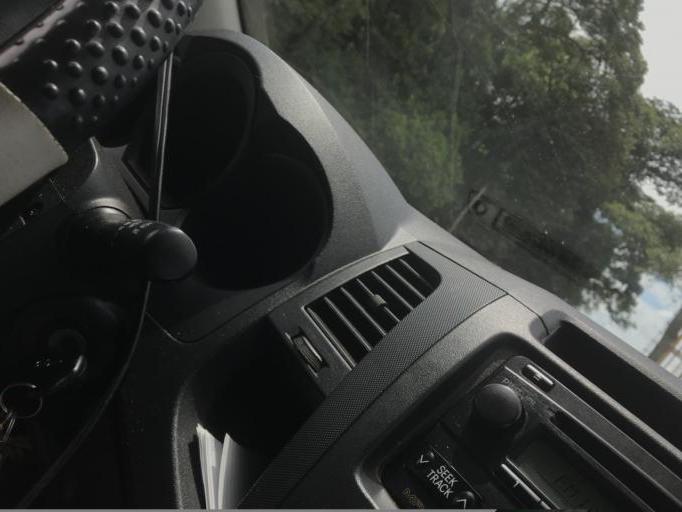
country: BR
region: Minas Gerais
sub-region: Patos De Minas
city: Patos de Minas
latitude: -18.6385
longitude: -46.4924
